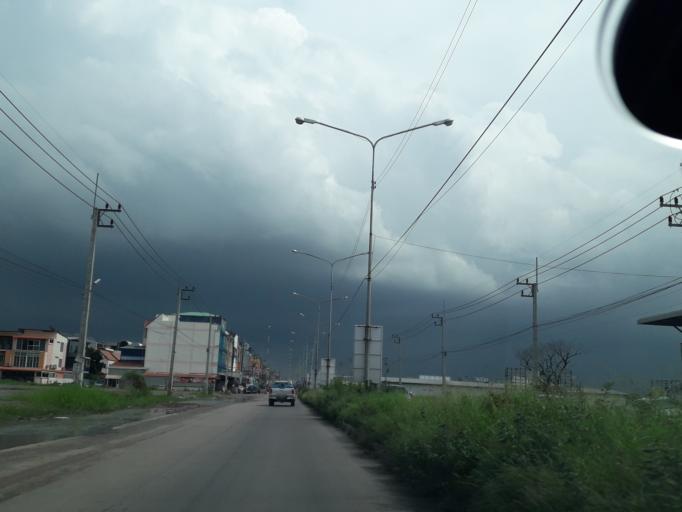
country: TH
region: Pathum Thani
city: Khlong Luang
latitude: 14.0760
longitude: 100.6340
